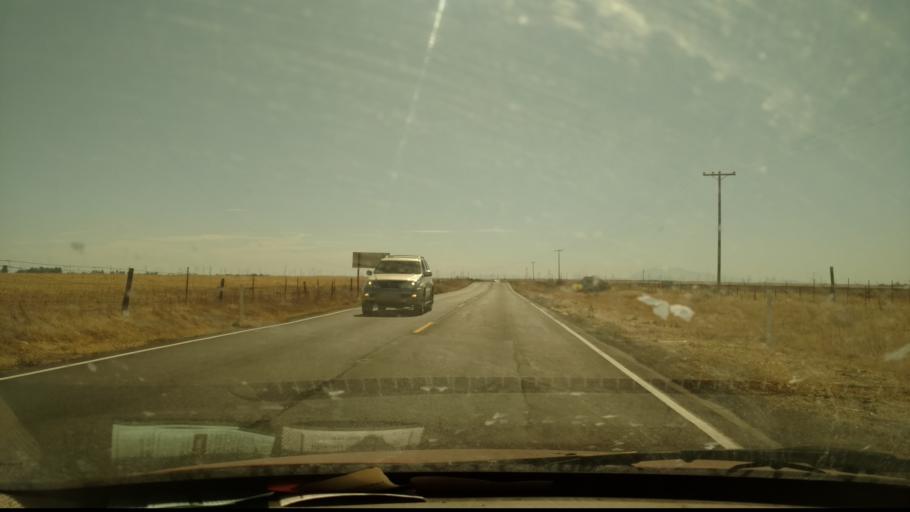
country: US
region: California
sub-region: Solano County
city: Rio Vista
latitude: 38.2387
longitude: -121.8057
